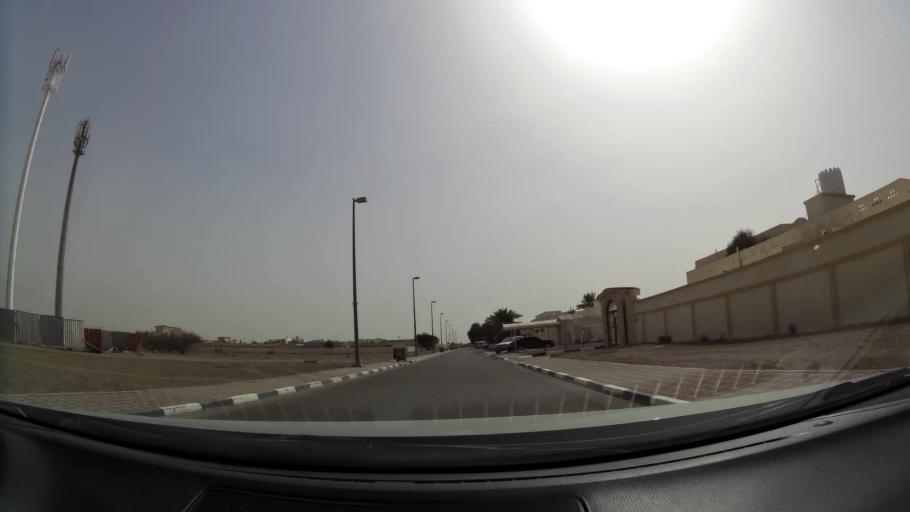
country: AE
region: Abu Dhabi
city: Al Ain
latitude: 24.1859
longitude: 55.6186
